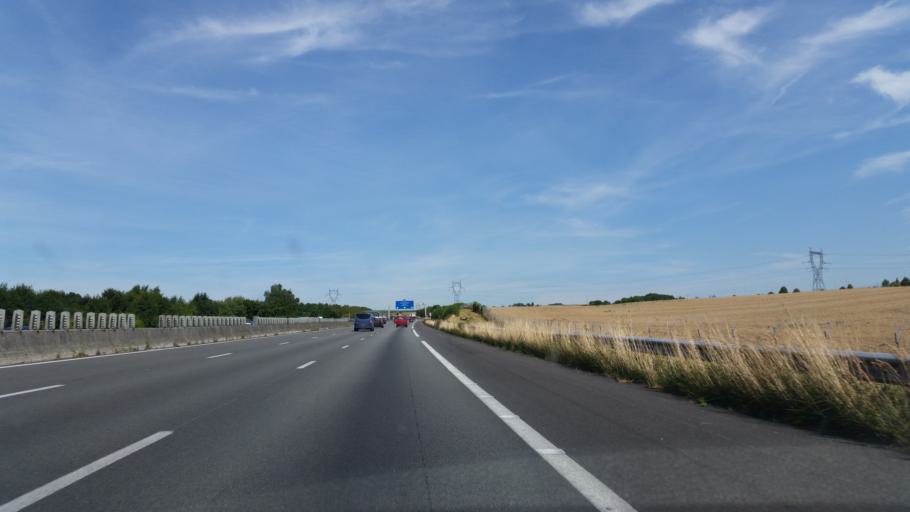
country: FR
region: Picardie
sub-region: Departement de la Somme
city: Peronne
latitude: 49.9636
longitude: 2.8576
